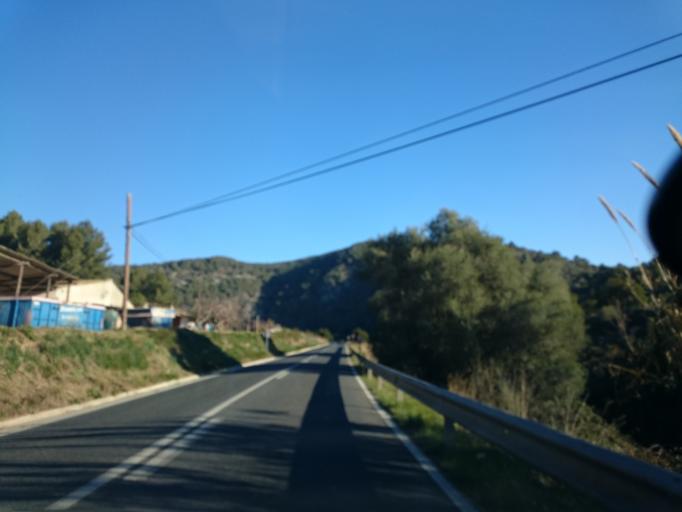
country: ES
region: Catalonia
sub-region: Provincia de Barcelona
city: Sant Pere de Ribes
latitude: 41.2689
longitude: 1.7661
